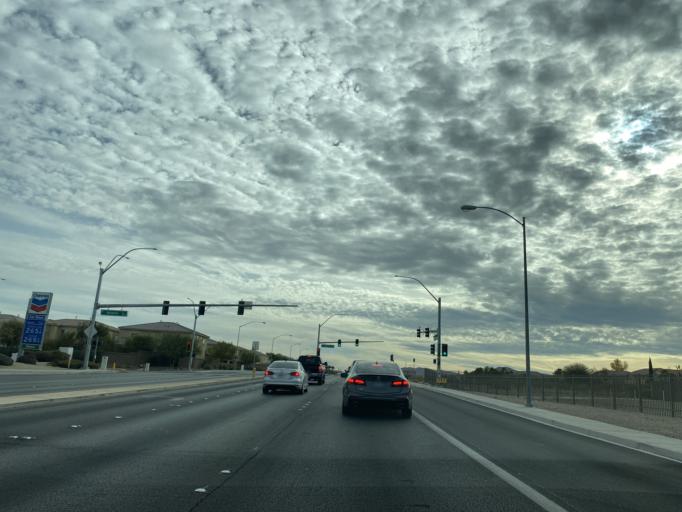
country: US
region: Nevada
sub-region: Clark County
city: Enterprise
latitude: 36.0416
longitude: -115.2791
